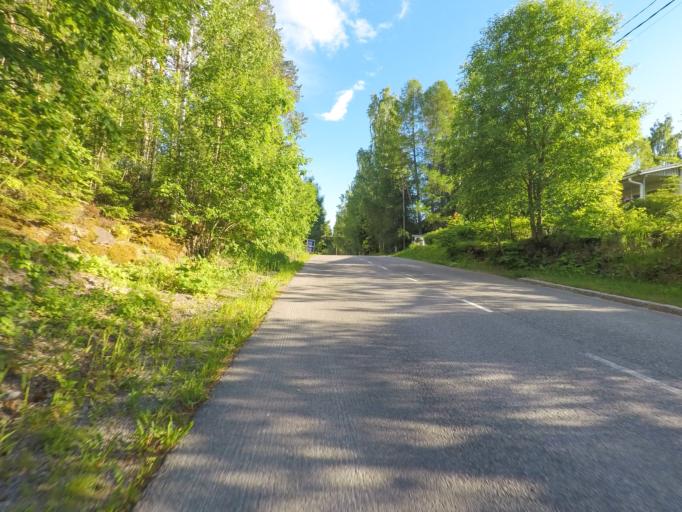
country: FI
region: Southern Savonia
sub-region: Savonlinna
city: Savonlinna
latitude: 61.8783
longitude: 28.8560
